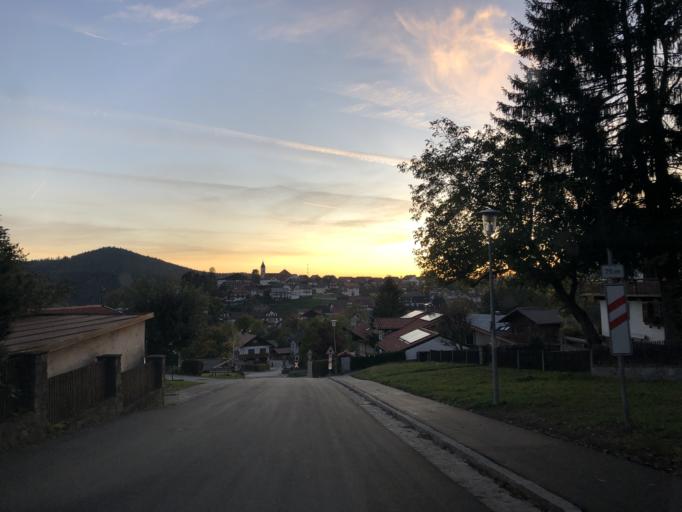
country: DE
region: Bavaria
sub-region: Lower Bavaria
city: Bodenmais
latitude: 49.0700
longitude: 13.1073
